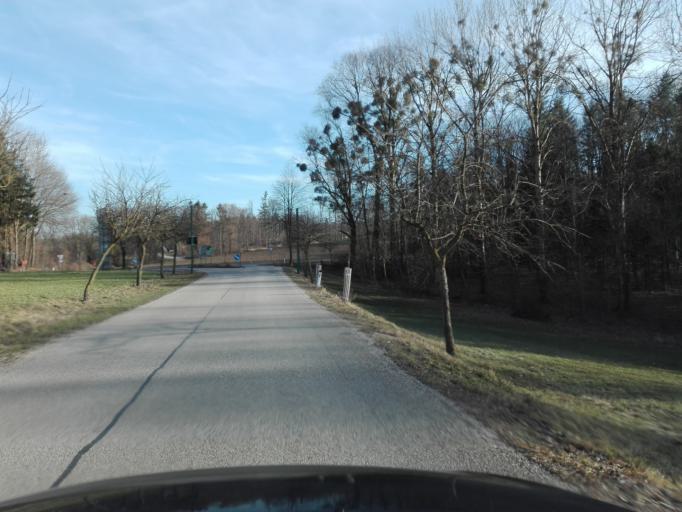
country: AT
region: Lower Austria
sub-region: Politischer Bezirk Amstetten
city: Amstetten
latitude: 48.1591
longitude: 14.8498
